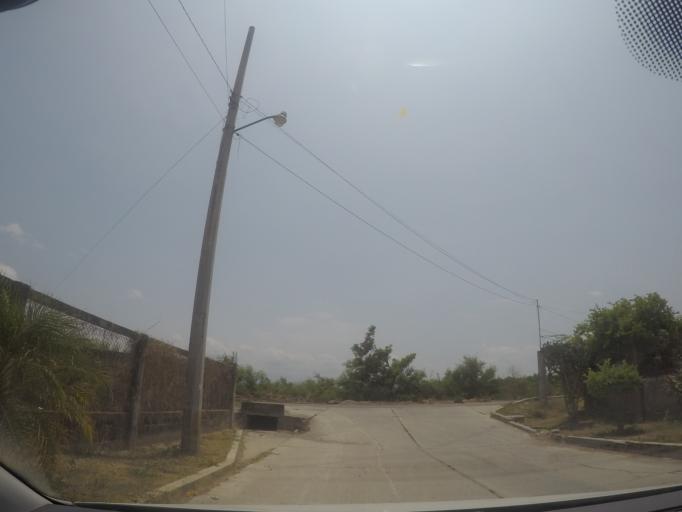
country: MX
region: Oaxaca
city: Asuncion Ixtaltepec
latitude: 16.5061
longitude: -95.0661
